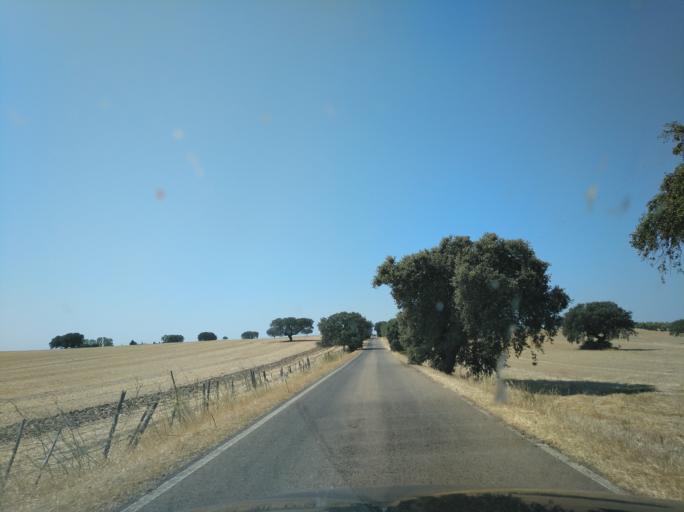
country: PT
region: Portalegre
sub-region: Campo Maior
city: Campo Maior
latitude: 39.0007
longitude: -6.9889
